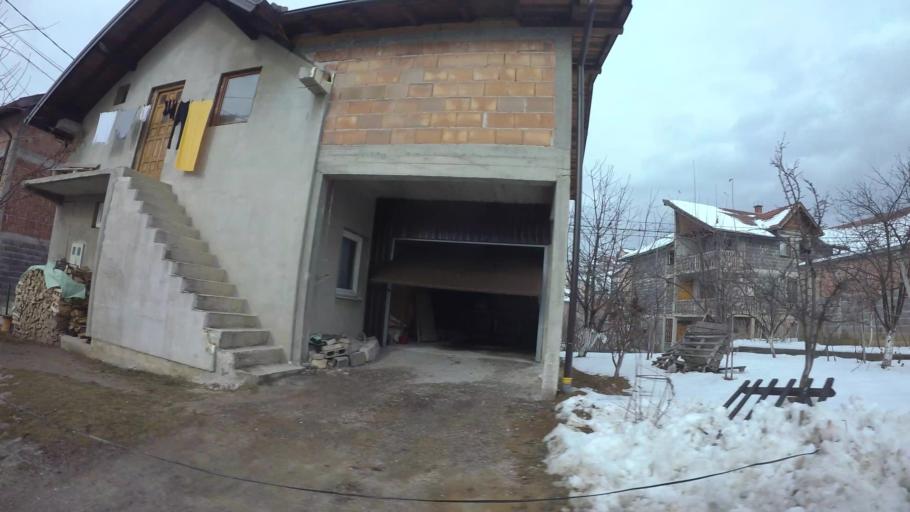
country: BA
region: Federation of Bosnia and Herzegovina
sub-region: Kanton Sarajevo
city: Sarajevo
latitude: 43.8595
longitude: 18.3286
